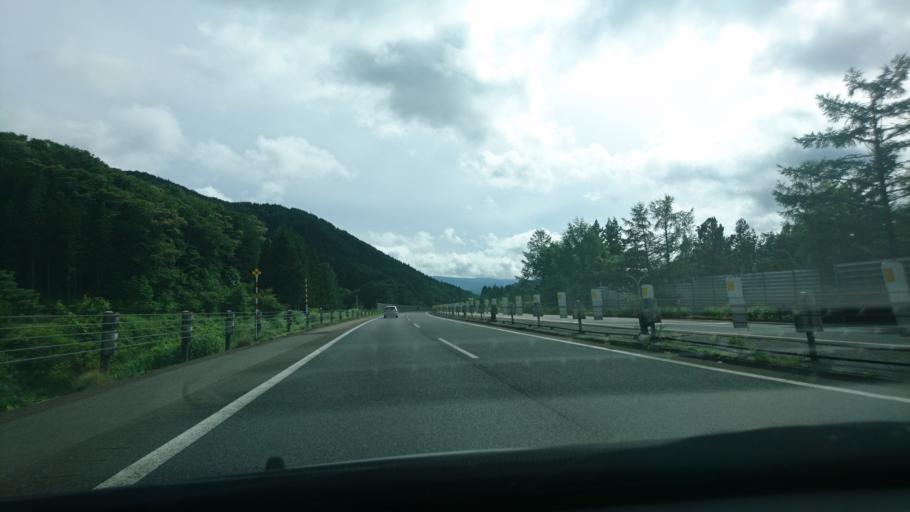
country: JP
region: Akita
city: Hanawa
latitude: 40.0520
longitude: 141.0142
